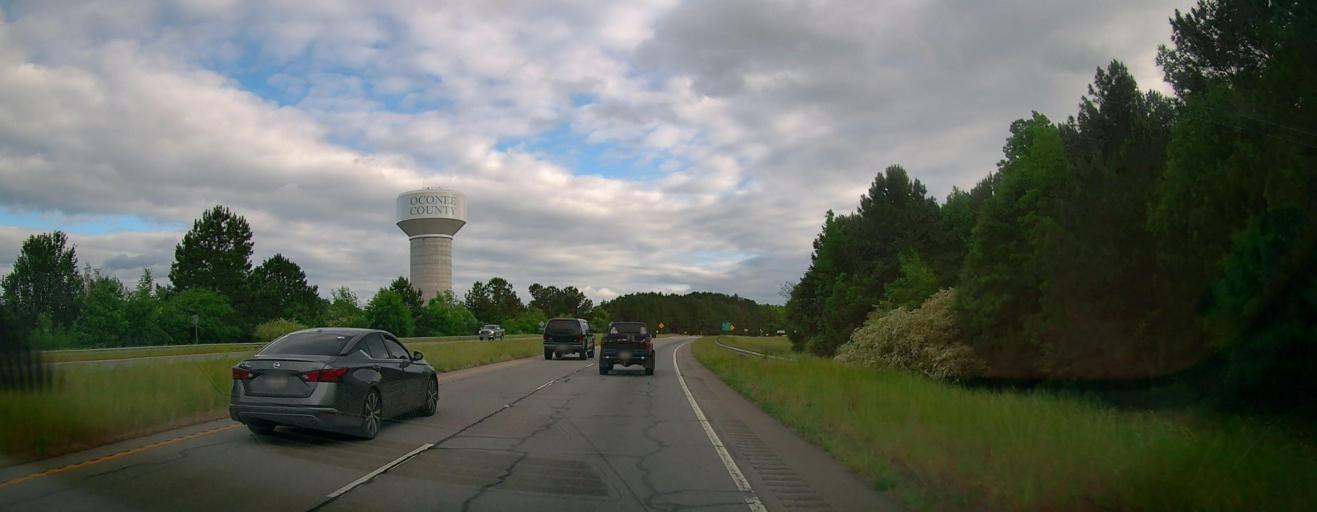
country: US
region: Georgia
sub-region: Oconee County
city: Watkinsville
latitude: 33.8485
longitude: -83.4226
